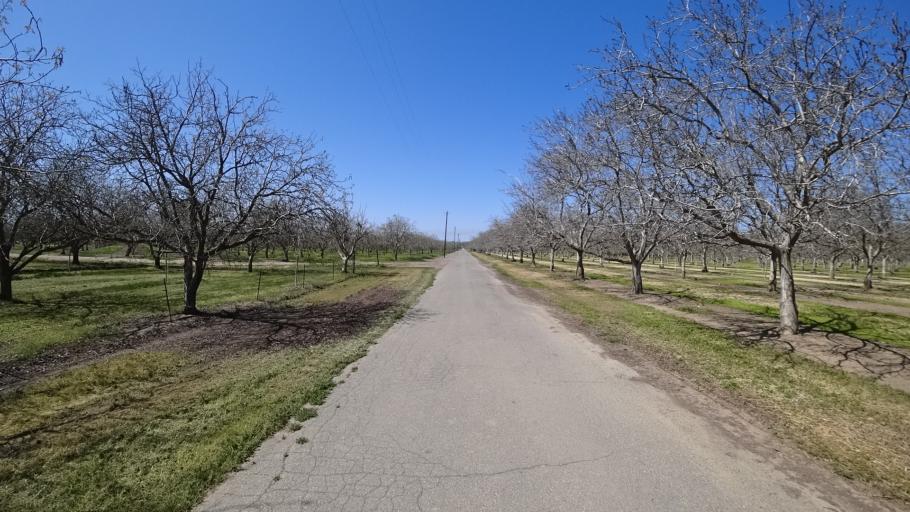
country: US
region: California
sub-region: Glenn County
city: Willows
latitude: 39.4435
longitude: -121.9791
